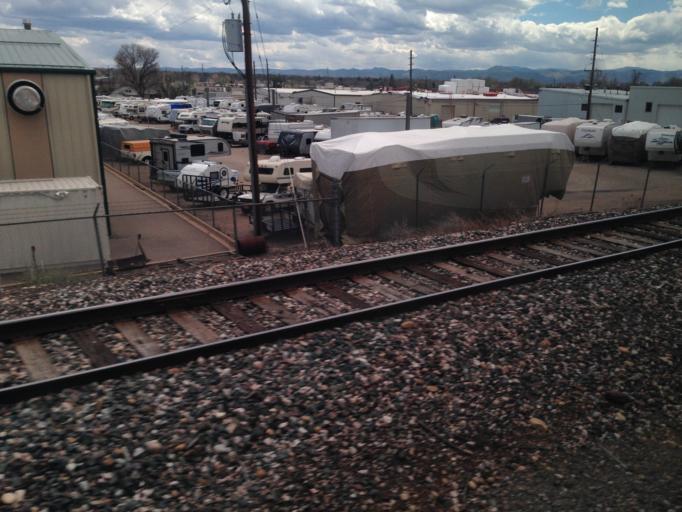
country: US
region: Colorado
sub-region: Jefferson County
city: Arvada
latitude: 39.8005
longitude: -105.0646
